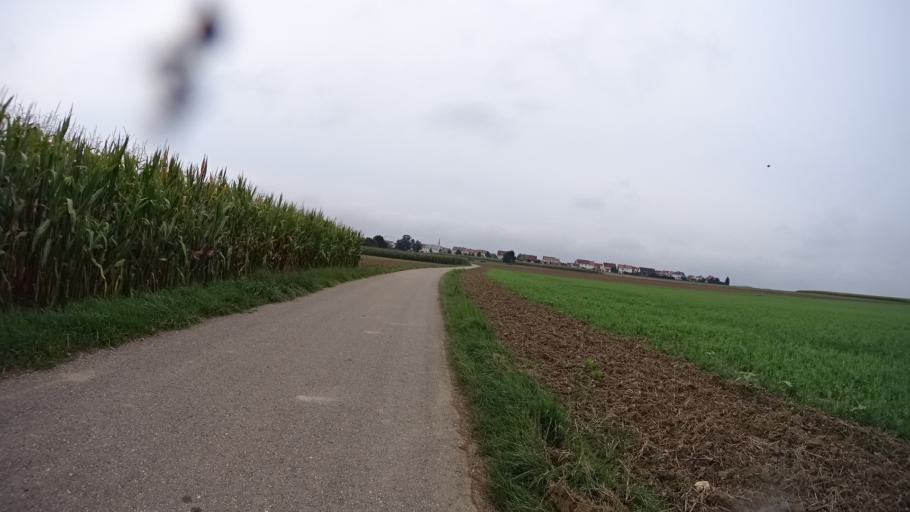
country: DE
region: Bavaria
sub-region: Upper Bavaria
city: Gaimersheim
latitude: 48.8201
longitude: 11.3647
